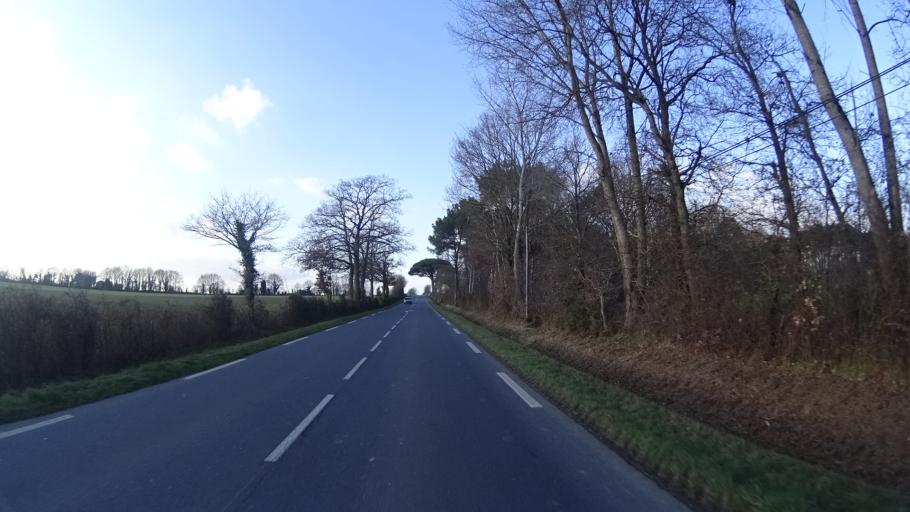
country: FR
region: Pays de la Loire
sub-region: Departement de la Loire-Atlantique
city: Fegreac
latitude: 47.5820
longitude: -1.9943
